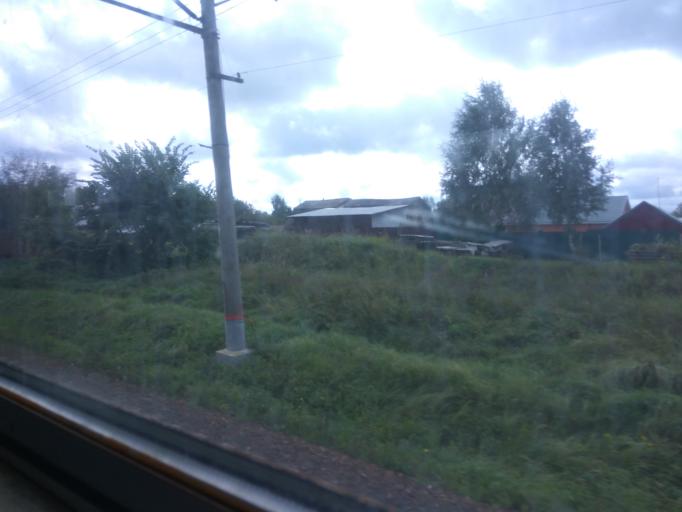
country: RU
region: Moskovskaya
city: Beloozerskiy
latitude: 55.4523
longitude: 38.4748
